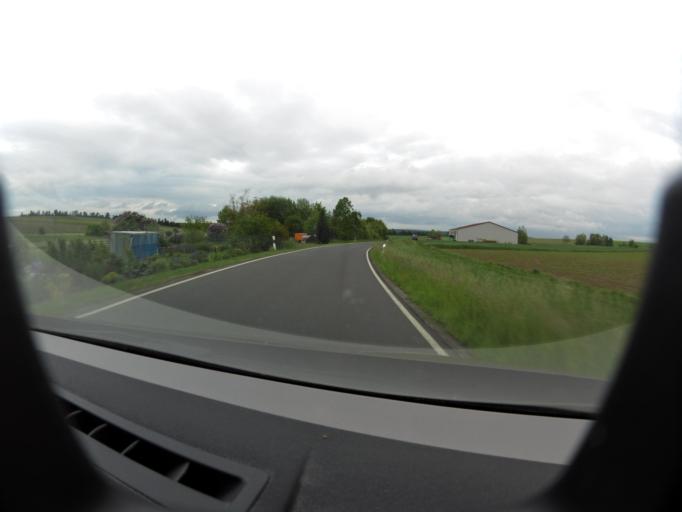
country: DE
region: Bavaria
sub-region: Regierungsbezirk Unterfranken
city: Volkach
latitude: 49.8883
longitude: 10.2309
